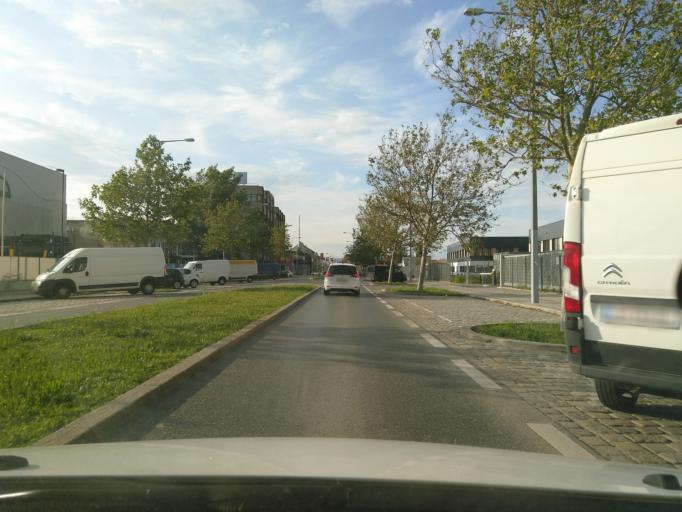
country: AT
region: Lower Austria
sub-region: Politischer Bezirk Modling
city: Brunn am Gebirge
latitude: 48.1395
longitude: 16.2982
